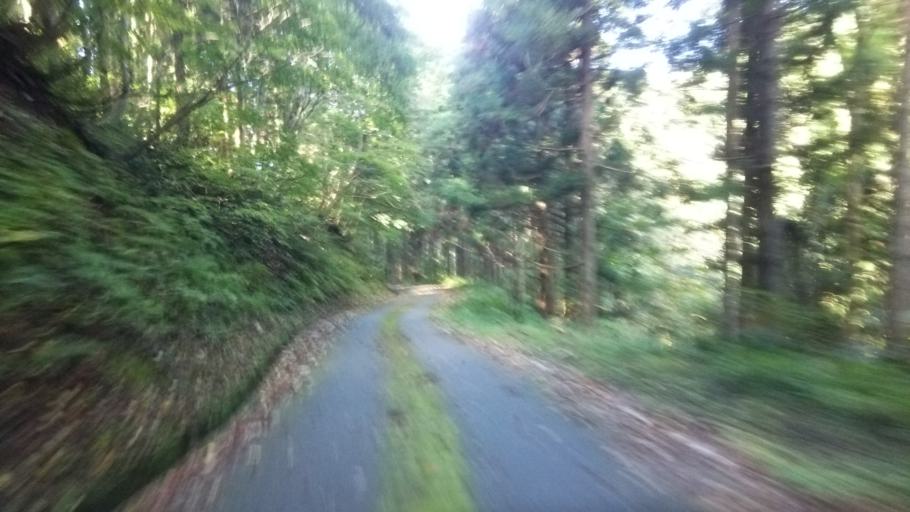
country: JP
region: Fukushima
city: Kitakata
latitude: 37.6129
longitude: 139.9703
